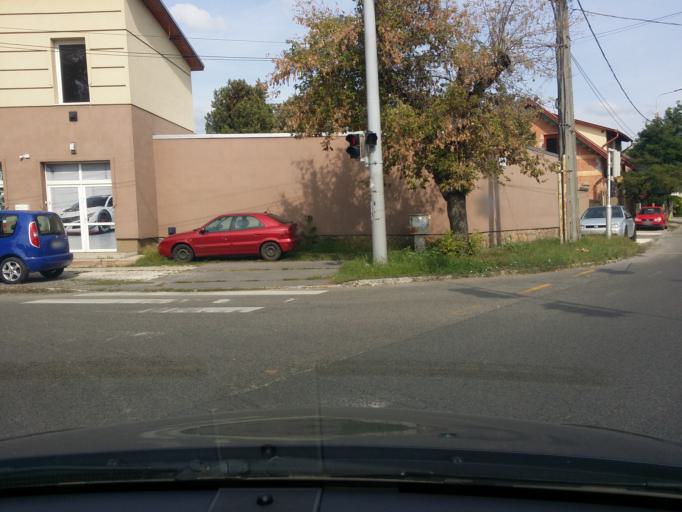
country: HU
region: Budapest
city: Budapest XV. keruelet
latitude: 47.5641
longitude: 19.1266
